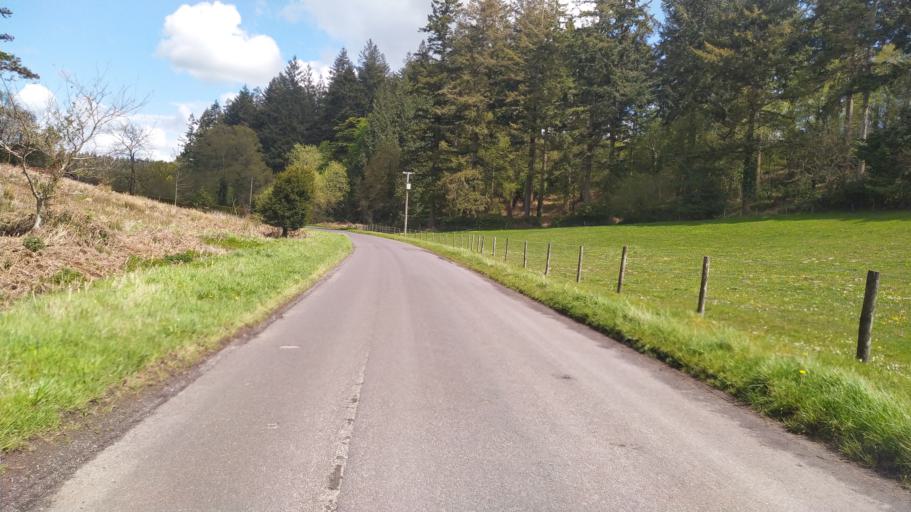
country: GB
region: England
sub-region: Wiltshire
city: Corsley
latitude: 51.1730
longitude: -2.2238
